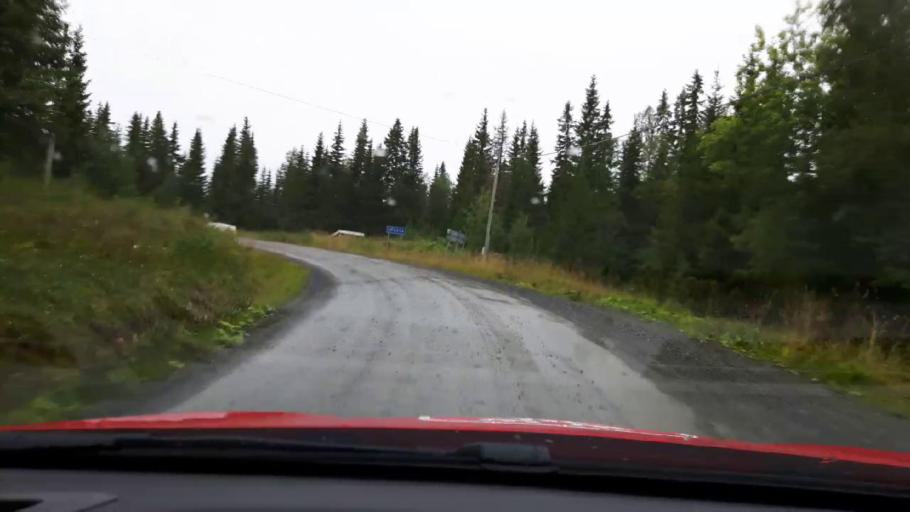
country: SE
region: Jaemtland
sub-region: Are Kommun
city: Are
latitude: 63.4328
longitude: 12.8015
